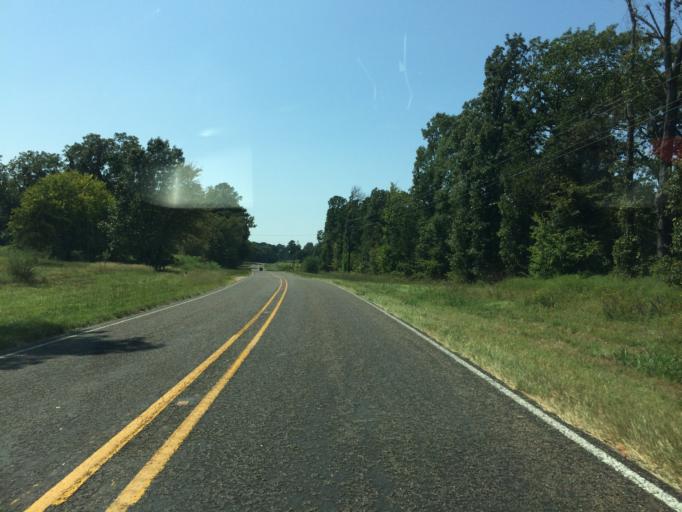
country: US
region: Texas
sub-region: Wood County
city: Mineola
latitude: 32.6793
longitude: -95.4376
